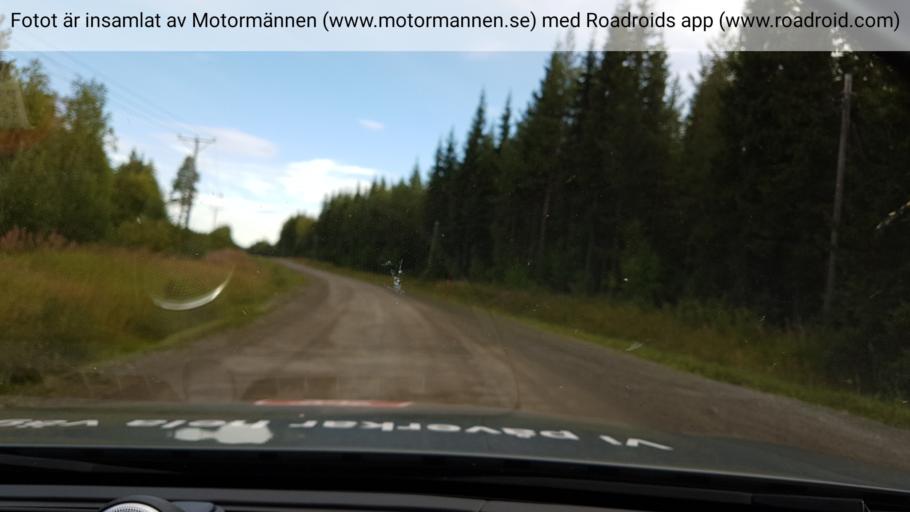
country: SE
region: Jaemtland
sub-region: Stroemsunds Kommun
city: Stroemsund
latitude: 63.9853
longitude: 15.8162
